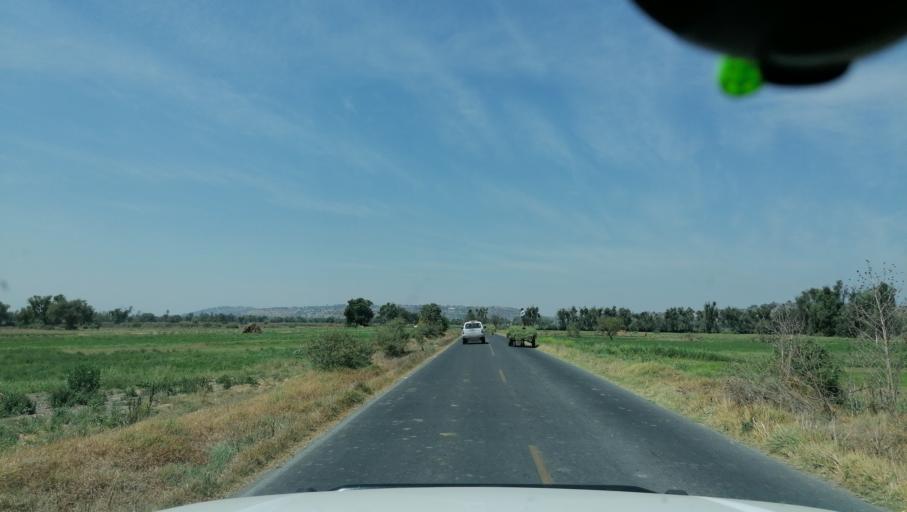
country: MX
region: Tlaxcala
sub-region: Tetlatlahuca
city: Tetlatlahuca
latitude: 19.2139
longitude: -98.2851
